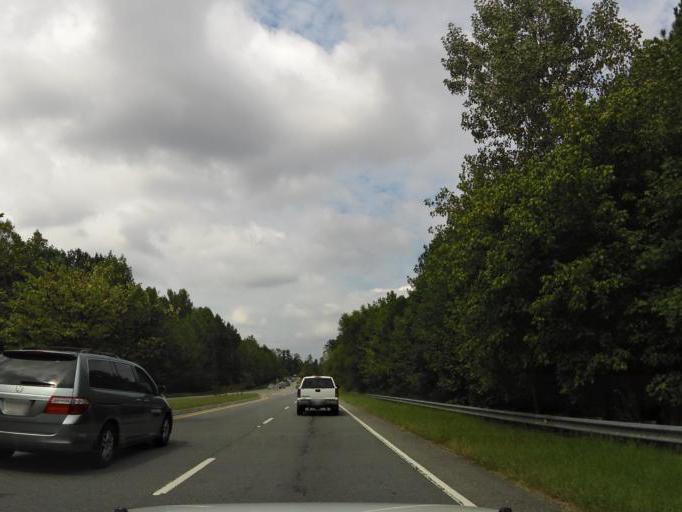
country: US
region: Georgia
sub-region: Cobb County
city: Powder Springs
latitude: 33.8845
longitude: -84.6373
